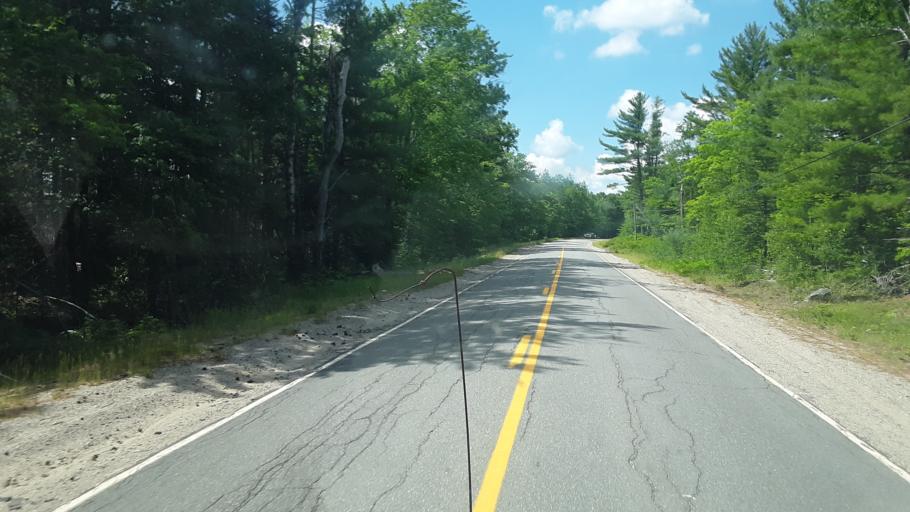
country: US
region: Maine
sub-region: Washington County
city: Machias
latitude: 44.8888
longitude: -67.6230
